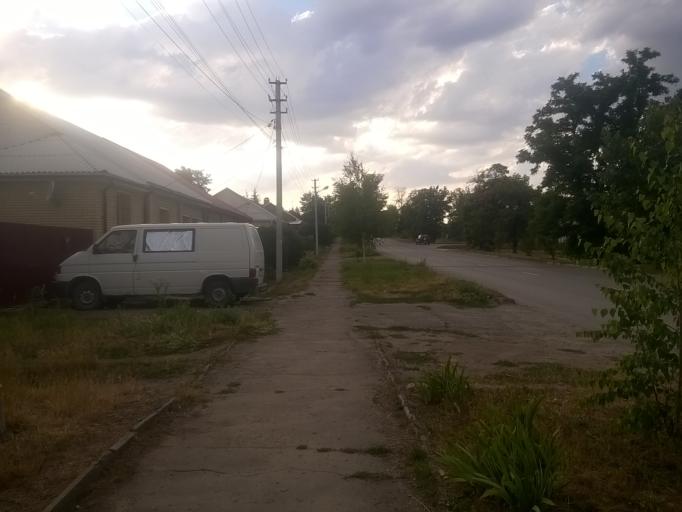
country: RU
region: Rostov
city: Donetsk
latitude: 48.3320
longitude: 39.9618
